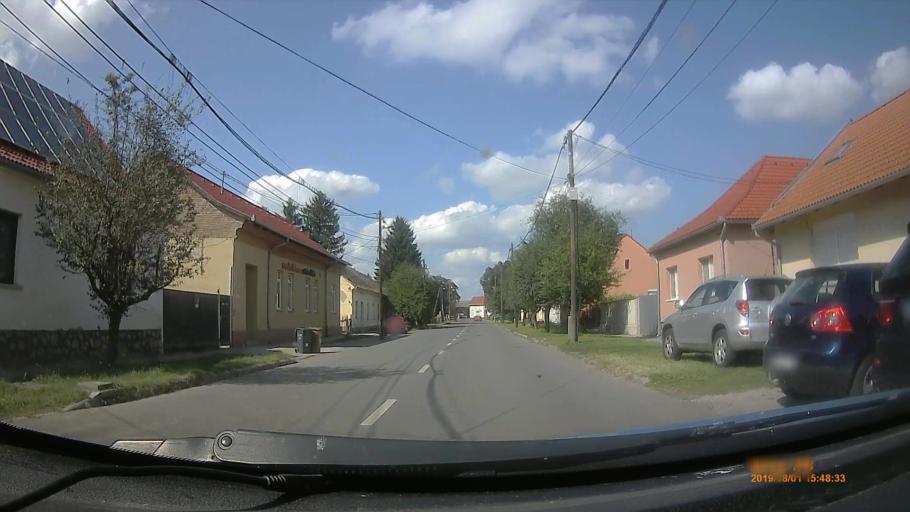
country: HU
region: Baranya
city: Szentlorinc
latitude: 46.0382
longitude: 17.9855
